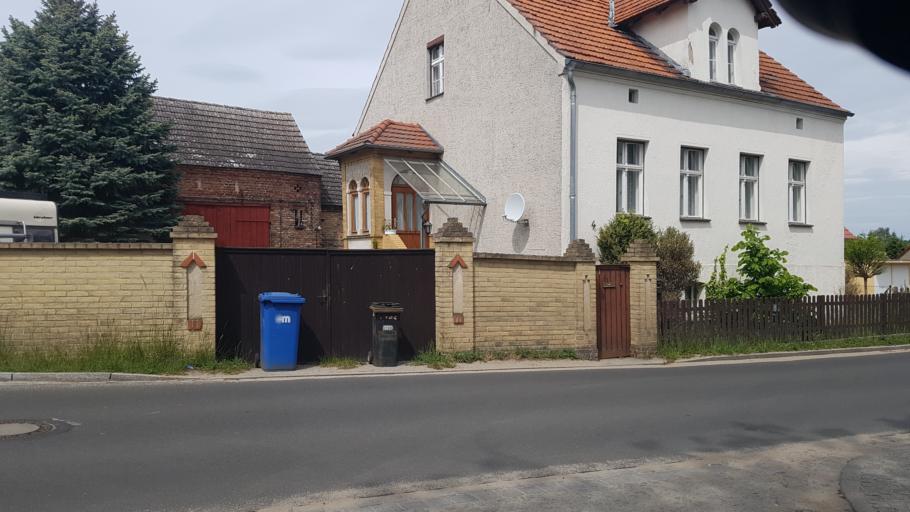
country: DE
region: Brandenburg
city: Michendorf
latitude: 52.3117
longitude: 13.0633
